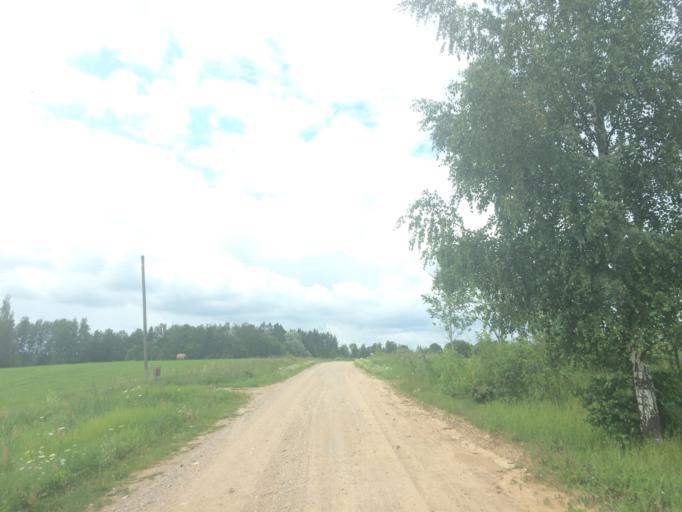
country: LV
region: Rezekne
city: Rezekne
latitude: 56.6593
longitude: 27.2709
